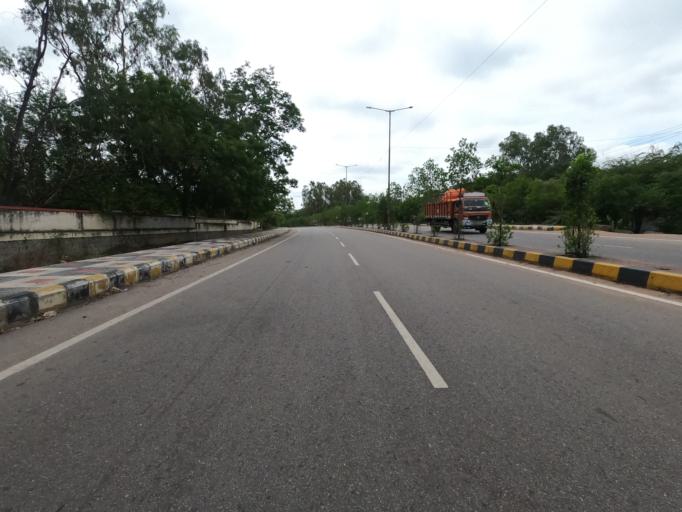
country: IN
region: Telangana
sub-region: Hyderabad
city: Hyderabad
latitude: 17.3197
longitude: 78.3925
